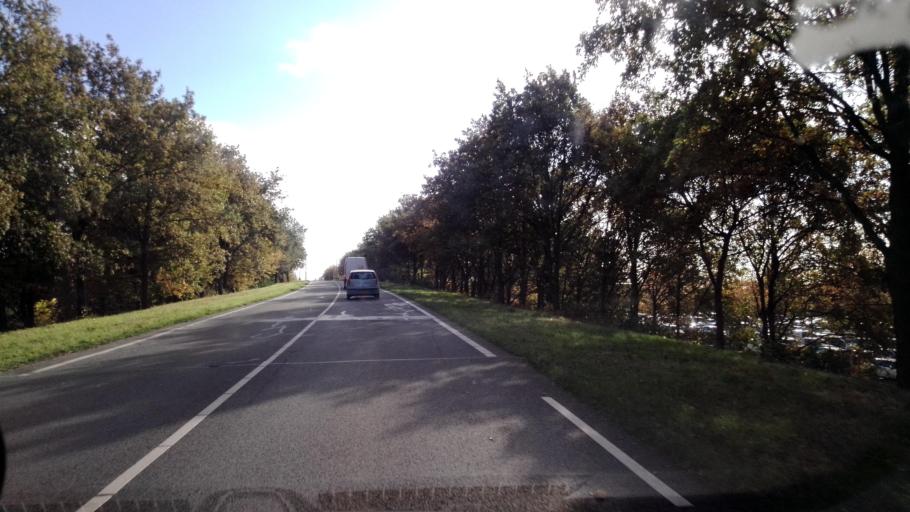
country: NL
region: Limburg
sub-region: Gemeente Venlo
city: Venlo
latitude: 51.3900
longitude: 6.1405
